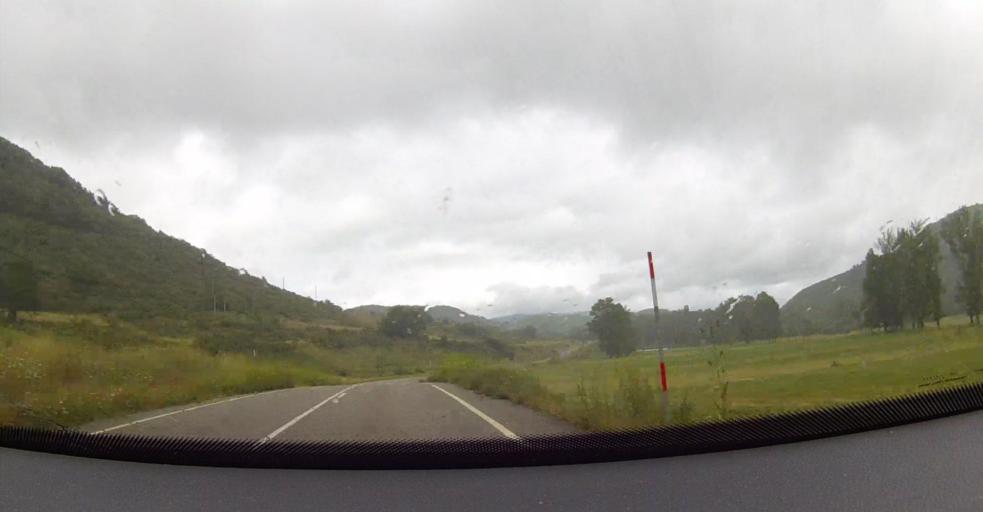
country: ES
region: Castille and Leon
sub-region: Provincia de Leon
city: Acebedo
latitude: 43.0391
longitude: -5.1026
